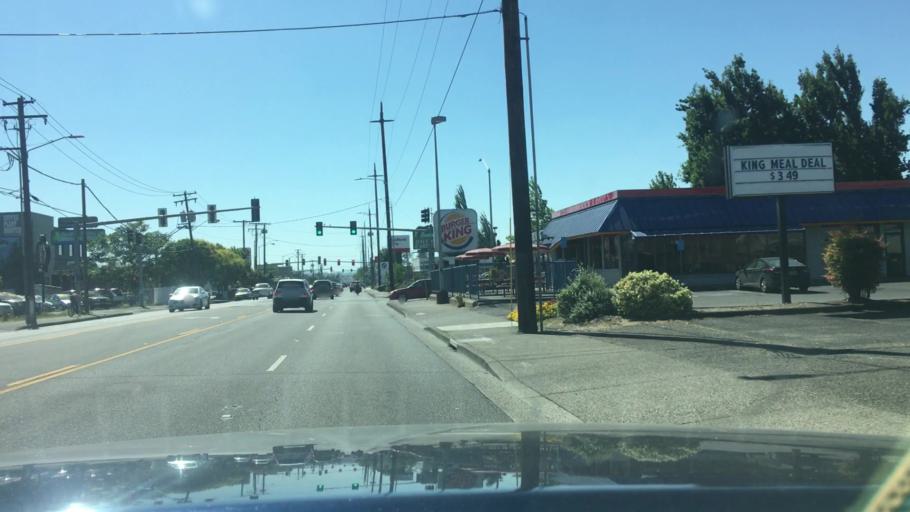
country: US
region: Oregon
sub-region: Lane County
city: Eugene
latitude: 44.0480
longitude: -123.1330
